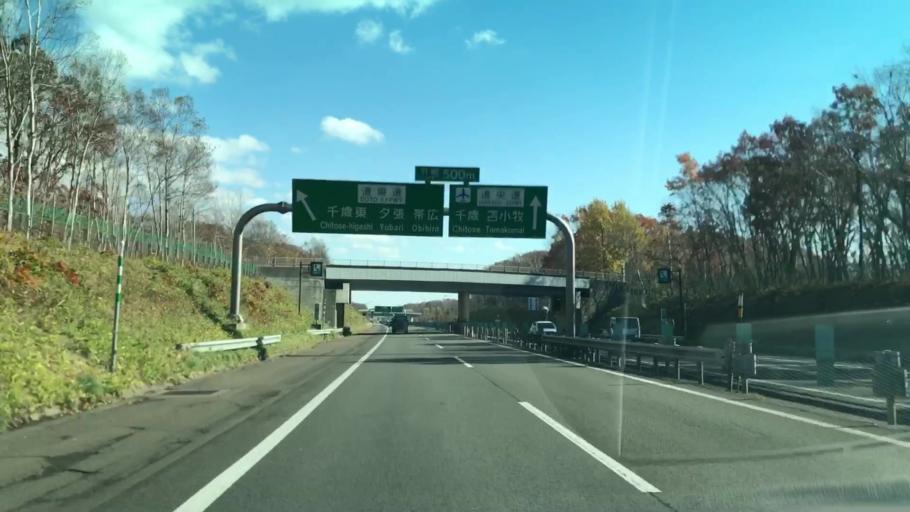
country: JP
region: Hokkaido
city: Chitose
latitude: 42.8482
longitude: 141.5764
